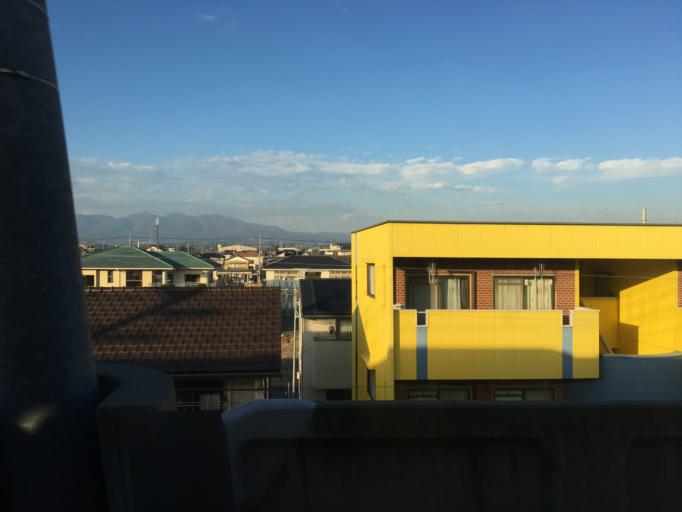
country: JP
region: Gunma
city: Isesaki
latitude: 36.3274
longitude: 139.1918
